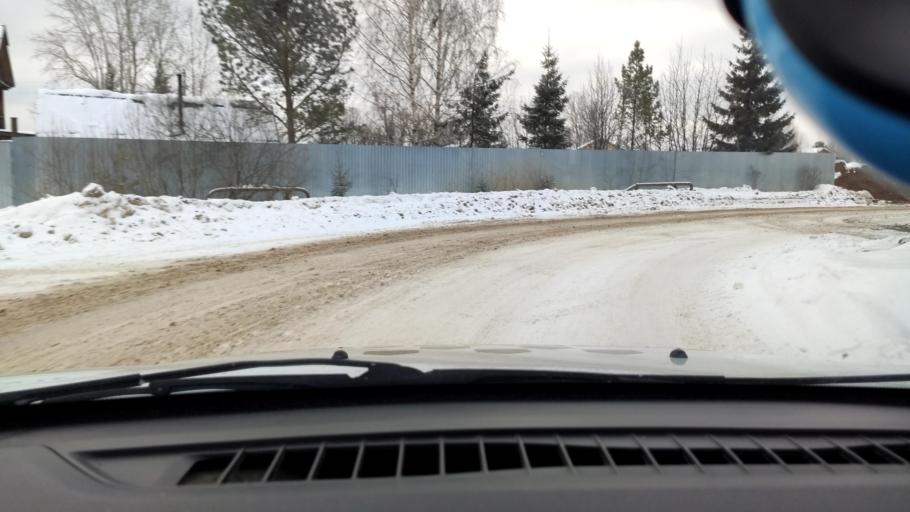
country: RU
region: Perm
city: Overyata
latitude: 58.0803
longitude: 55.9707
